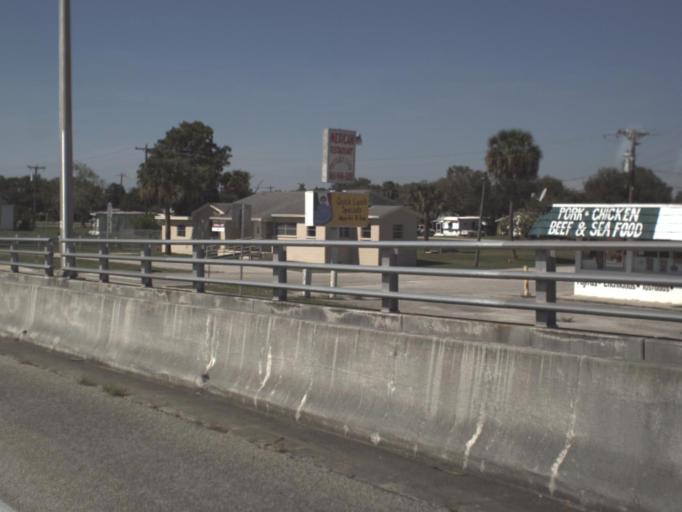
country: US
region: Florida
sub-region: Glades County
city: Moore Haven
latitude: 26.8335
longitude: -81.0939
